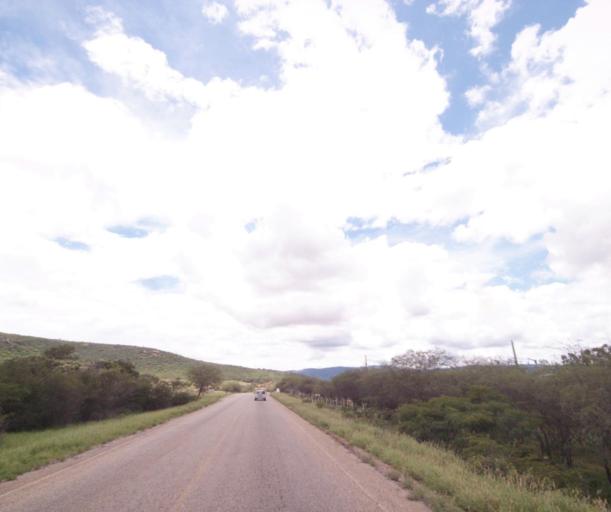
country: BR
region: Bahia
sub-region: Brumado
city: Brumado
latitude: -14.1993
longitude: -41.5992
